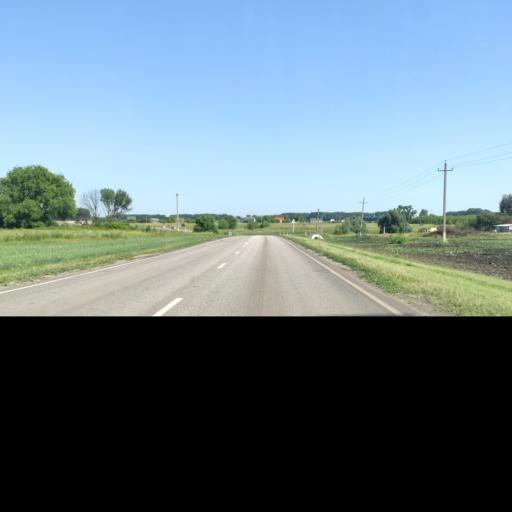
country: RU
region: Voronezj
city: Panino
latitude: 51.6521
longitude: 40.0112
